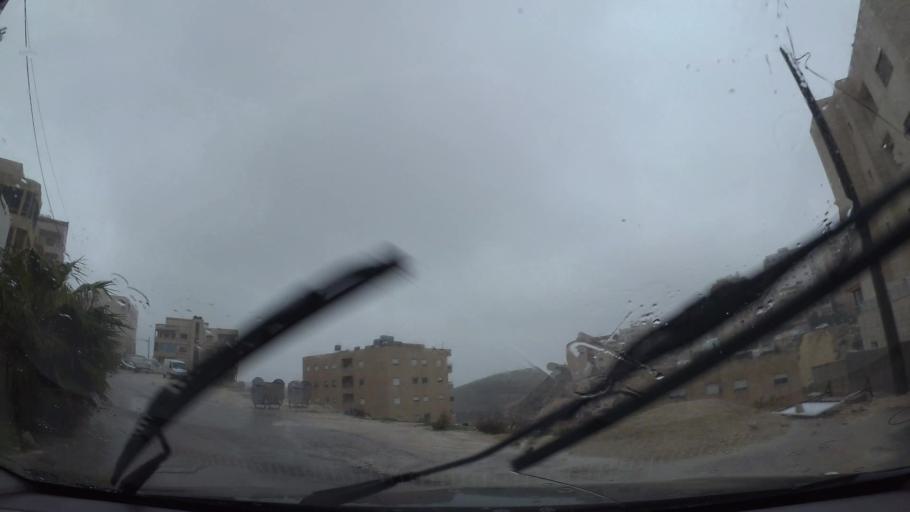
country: JO
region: Amman
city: Al Jubayhah
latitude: 32.0102
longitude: 35.8873
